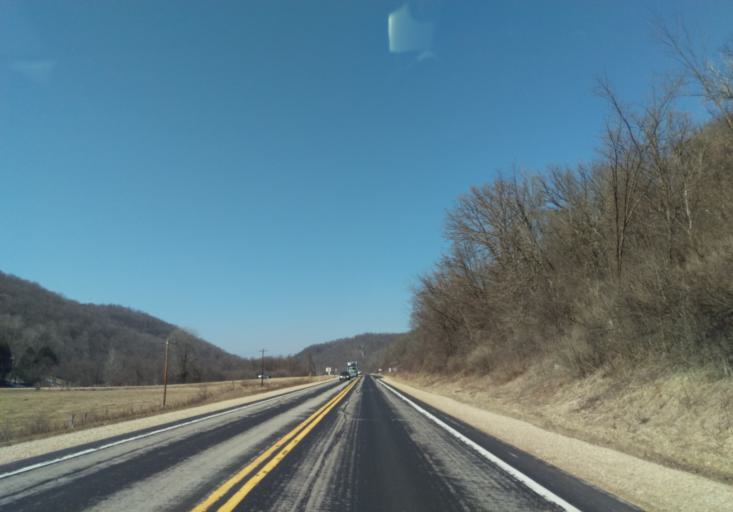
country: US
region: Wisconsin
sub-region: Vernon County
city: Viroqua
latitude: 43.4471
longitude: -90.7759
